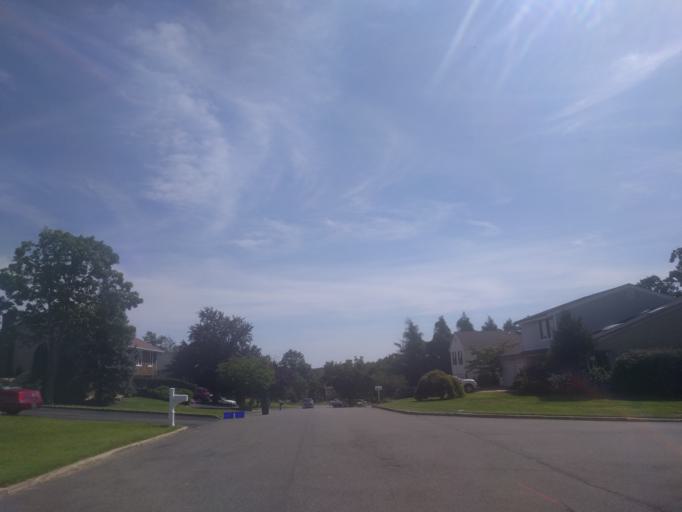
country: US
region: New York
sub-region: Nassau County
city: Glen Cove
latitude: 40.8783
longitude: -73.6214
